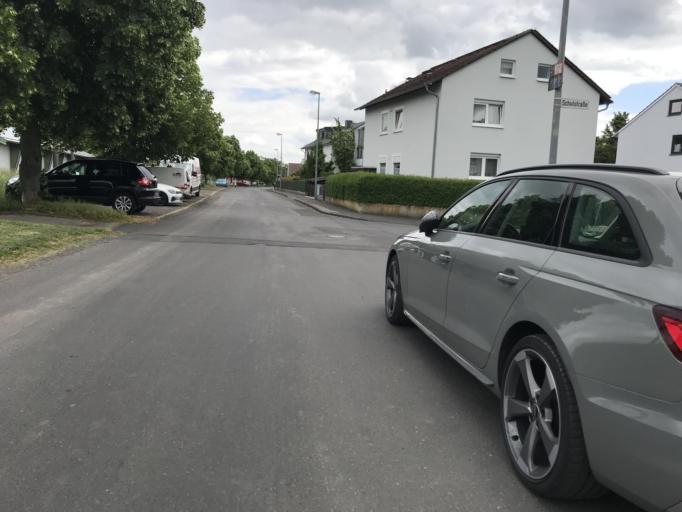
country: DE
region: Hesse
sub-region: Regierungsbezirk Kassel
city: Baunatal
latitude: 51.2528
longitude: 9.3871
